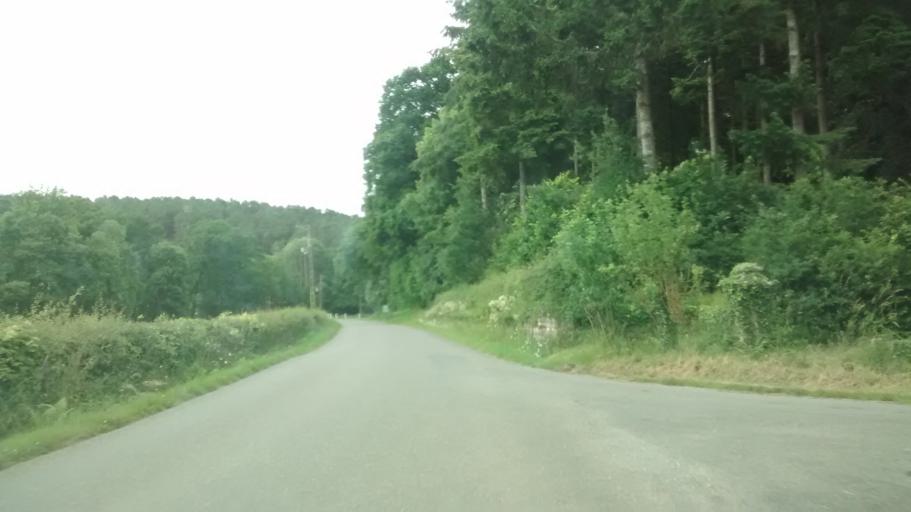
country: FR
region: Brittany
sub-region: Departement du Morbihan
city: Ruffiac
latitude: 47.8406
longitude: -2.2081
